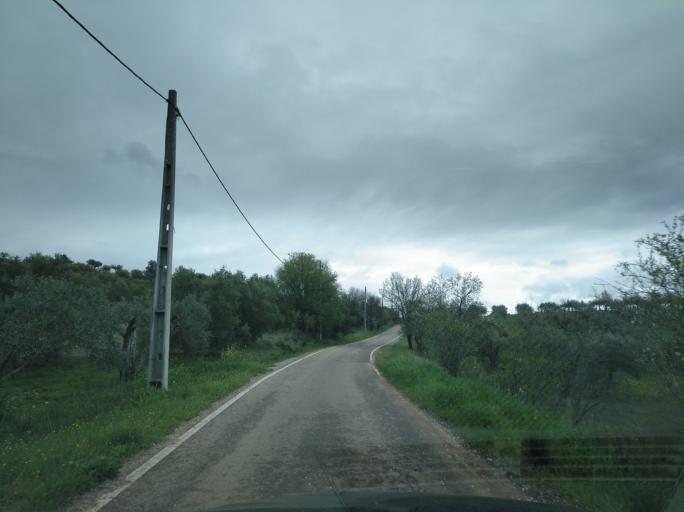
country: PT
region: Portalegre
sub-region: Campo Maior
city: Campo Maior
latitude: 38.9907
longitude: -7.0471
